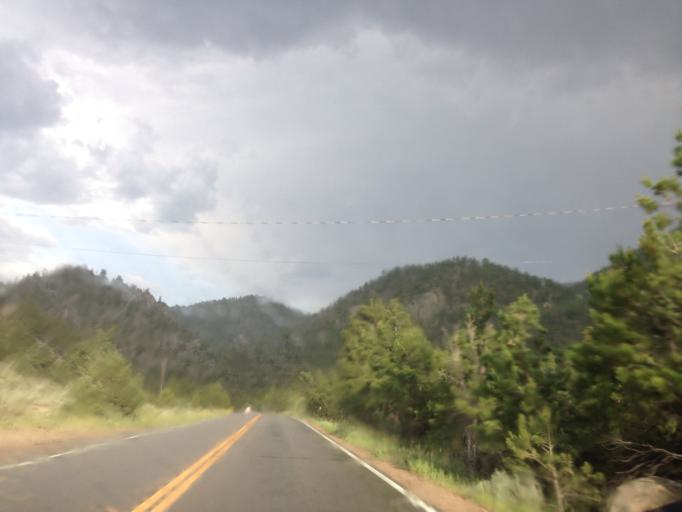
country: US
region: Colorado
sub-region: Larimer County
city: Estes Park
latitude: 40.6962
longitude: -105.6835
